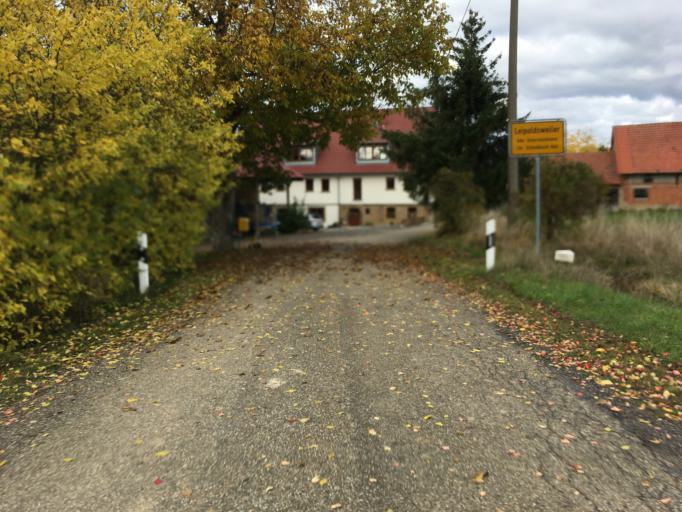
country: DE
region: Baden-Wuerttemberg
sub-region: Regierungsbezirk Stuttgart
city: Untermunkheim
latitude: 49.1891
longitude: 9.7418
